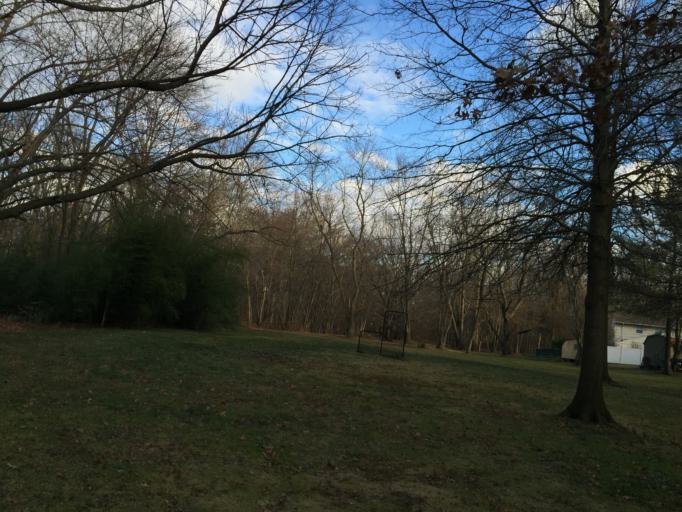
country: US
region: New Jersey
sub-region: Union County
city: New Providence
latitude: 40.7075
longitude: -74.4119
